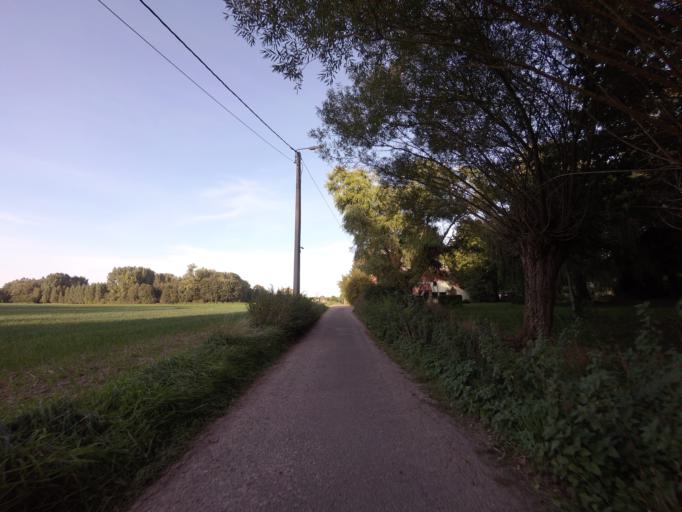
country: BE
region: Flanders
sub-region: Provincie Vlaams-Brabant
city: Boortmeerbeek
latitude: 50.9423
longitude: 4.5932
